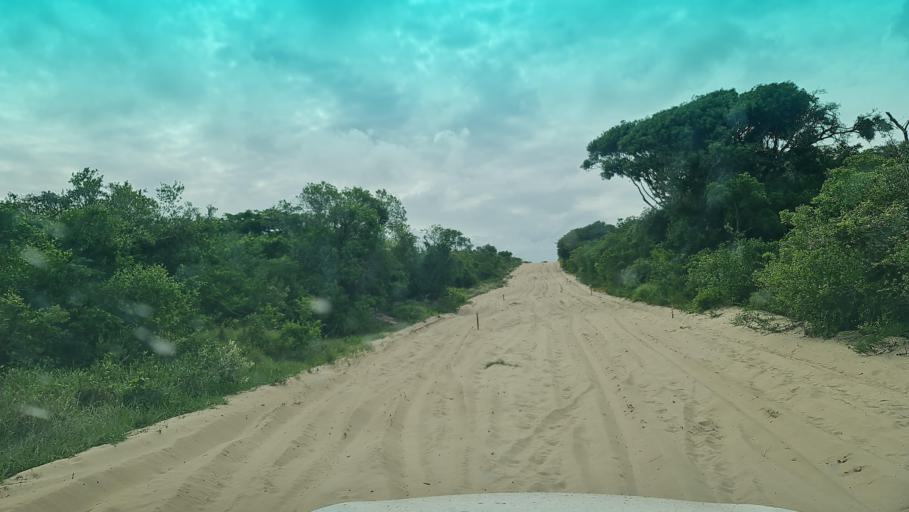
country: MZ
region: Maputo
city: Manhica
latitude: -25.4378
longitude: 32.9183
